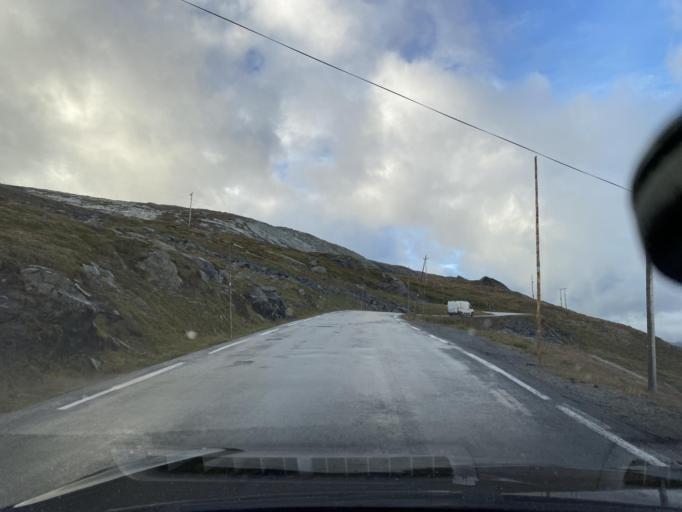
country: NO
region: Sogn og Fjordane
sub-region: Ardal
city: Farnes
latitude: 61.5717
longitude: 8.0295
